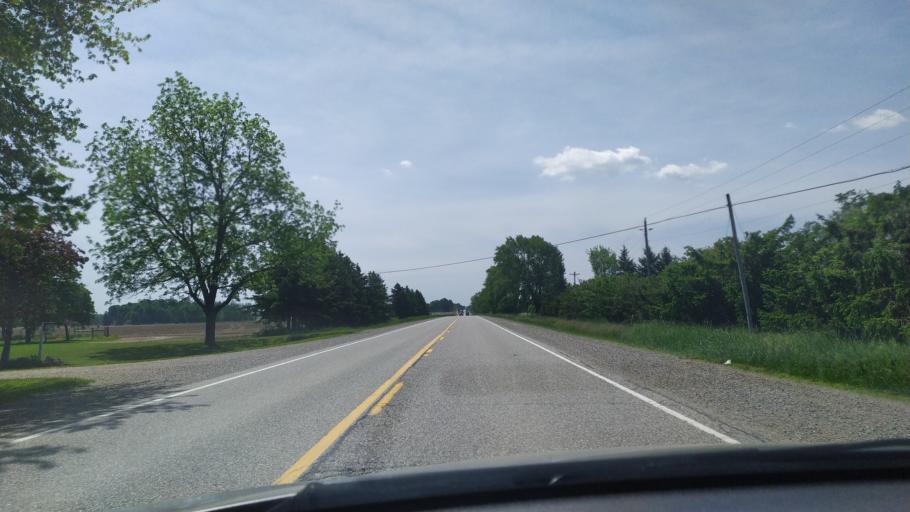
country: CA
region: Ontario
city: Dorchester
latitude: 43.1192
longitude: -81.0201
